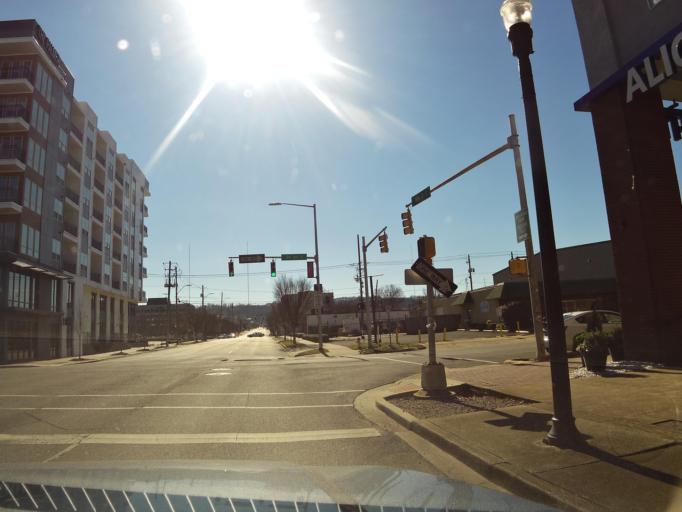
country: US
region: Alabama
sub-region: Jefferson County
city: Birmingham
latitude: 33.5061
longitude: -86.8112
